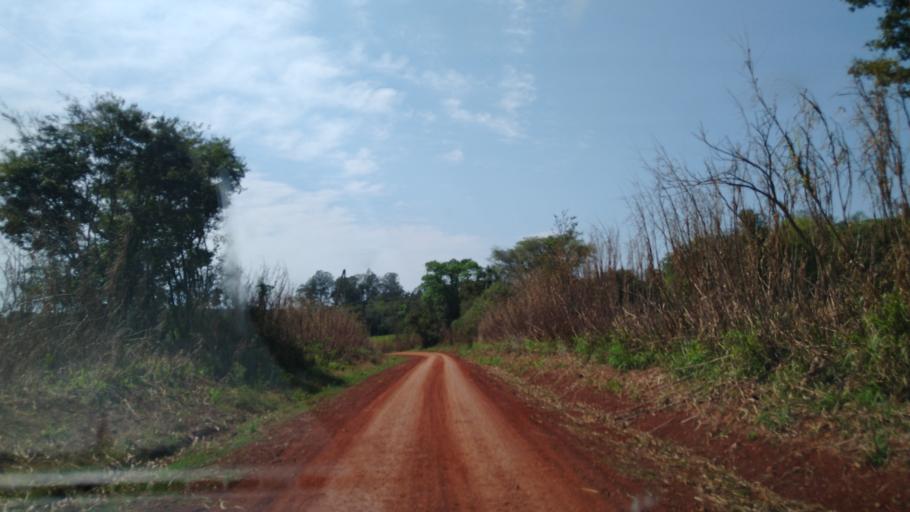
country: AR
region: Misiones
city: Capiovi
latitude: -26.9424
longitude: -55.0658
